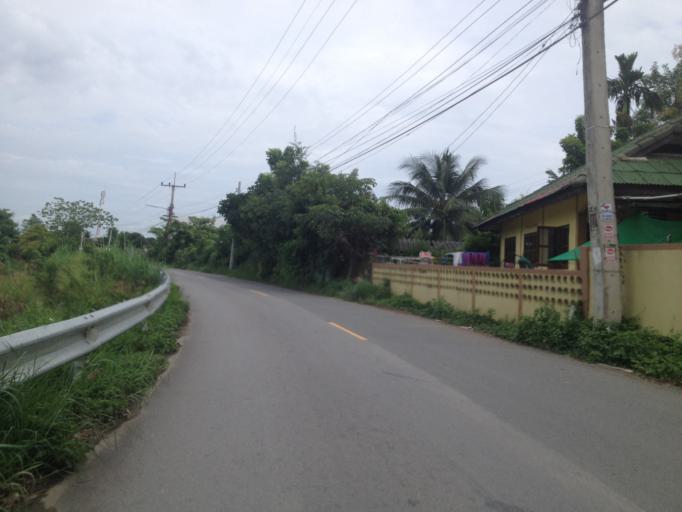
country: TH
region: Chiang Mai
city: Hang Dong
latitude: 18.7074
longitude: 98.9567
